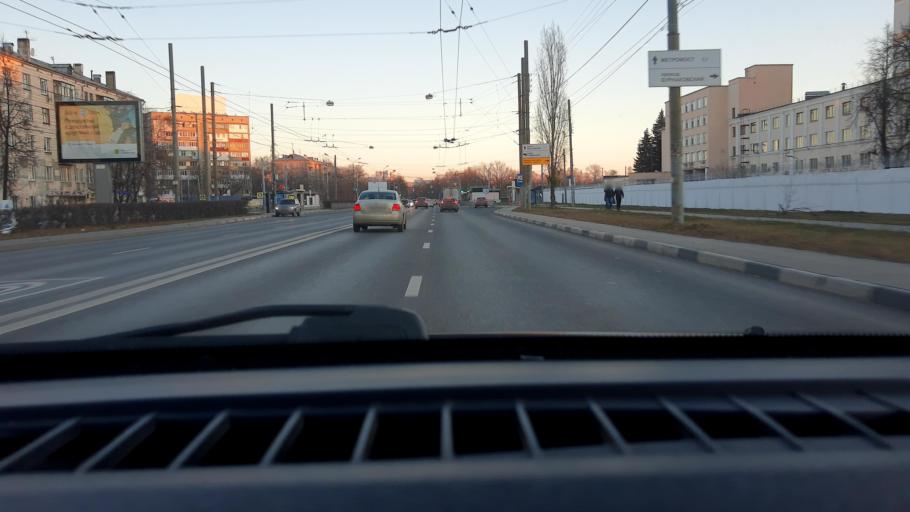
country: RU
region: Nizjnij Novgorod
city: Nizhniy Novgorod
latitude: 56.3254
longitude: 43.9111
